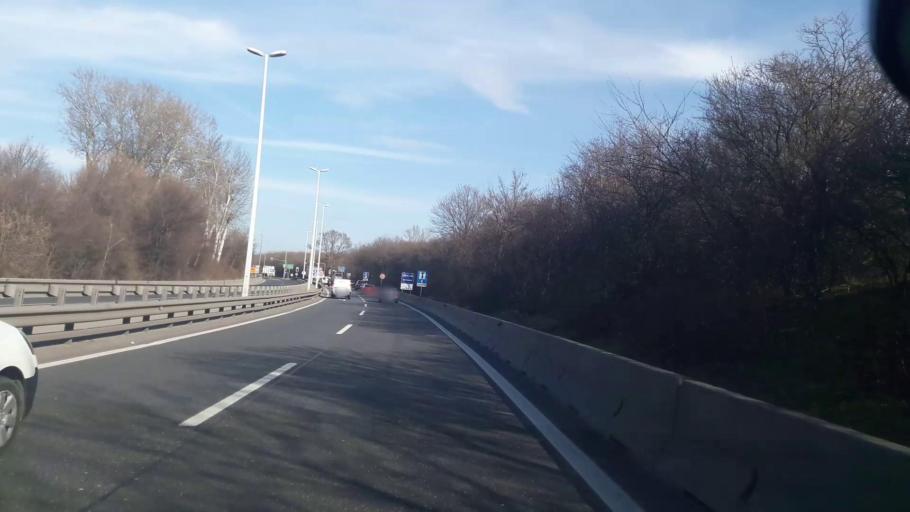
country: AT
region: Lower Austria
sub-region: Politischer Bezirk Korneuburg
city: Langenzersdorf
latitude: 48.2811
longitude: 16.3728
